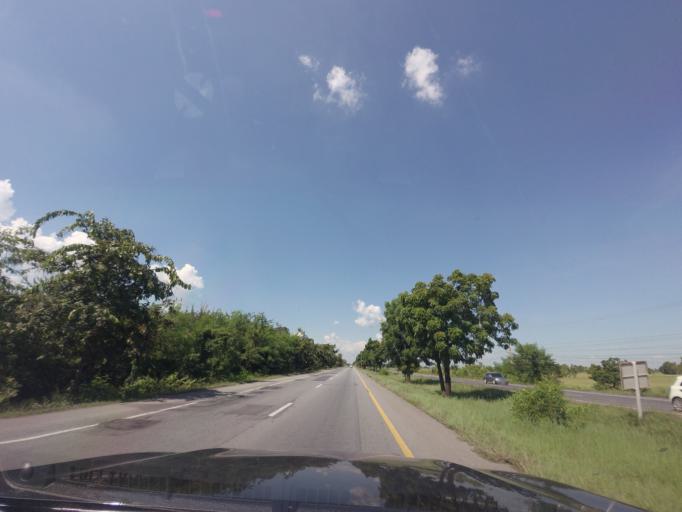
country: TH
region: Nakhon Ratchasima
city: Non Sung
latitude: 15.2042
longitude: 102.3536
